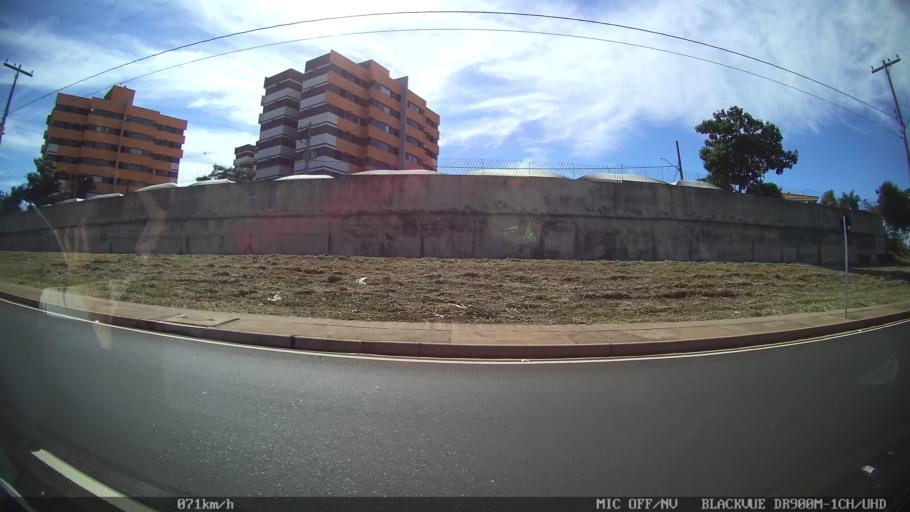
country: BR
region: Sao Paulo
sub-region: Sao Jose Do Rio Preto
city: Sao Jose do Rio Preto
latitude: -20.8502
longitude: -49.3906
